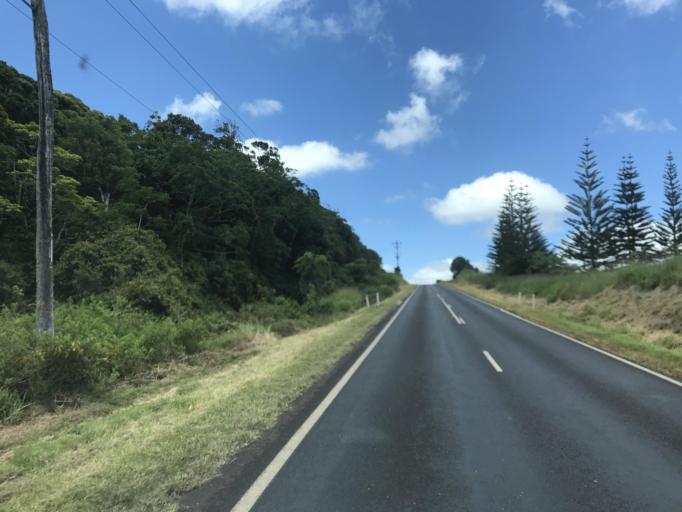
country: AU
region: Queensland
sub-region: Tablelands
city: Ravenshoe
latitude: -17.4998
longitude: 145.4767
